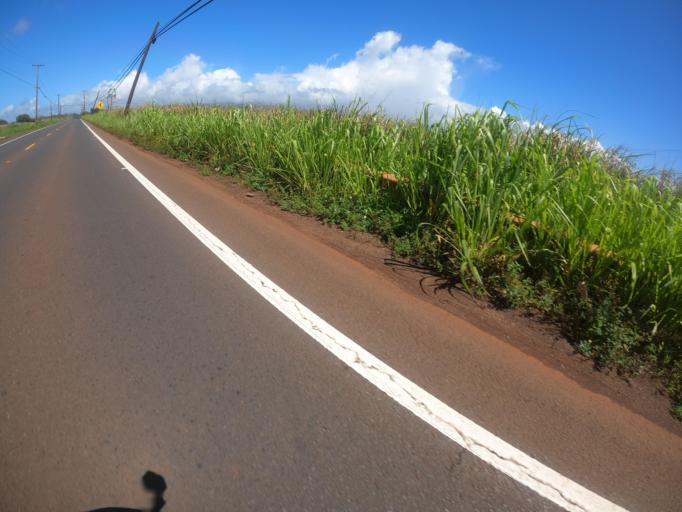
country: US
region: Hawaii
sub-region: Honolulu County
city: Schofield Barracks
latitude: 21.4694
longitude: -158.0534
